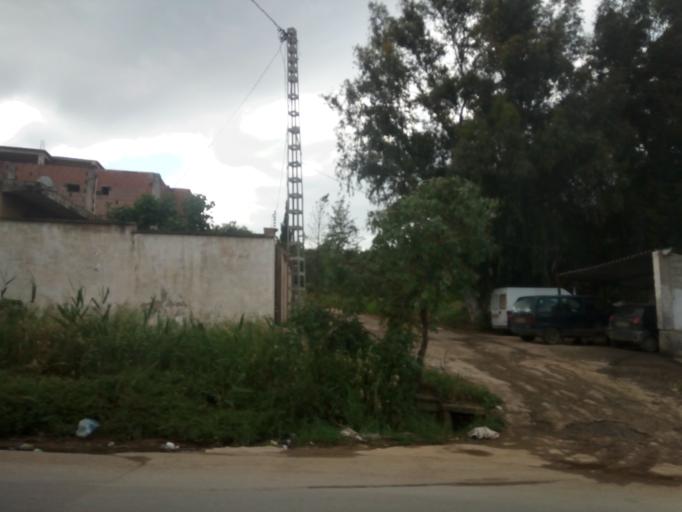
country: DZ
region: Tipaza
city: Douera
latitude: 36.6815
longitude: 2.9577
